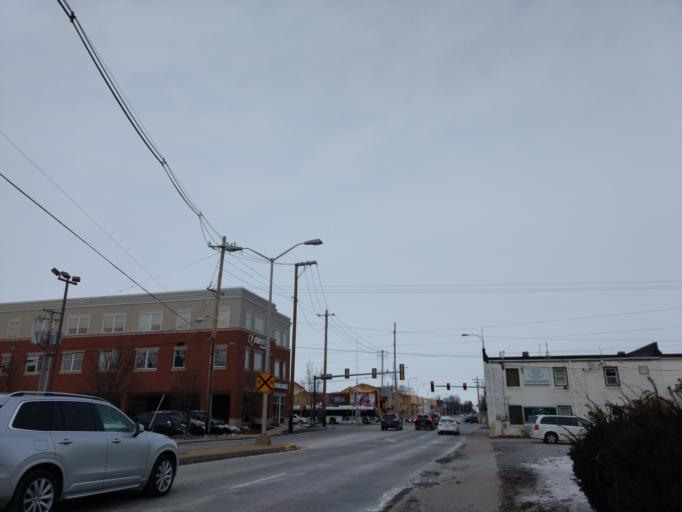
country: US
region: Illinois
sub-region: Champaign County
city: Urbana
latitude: 40.1156
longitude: -88.2192
